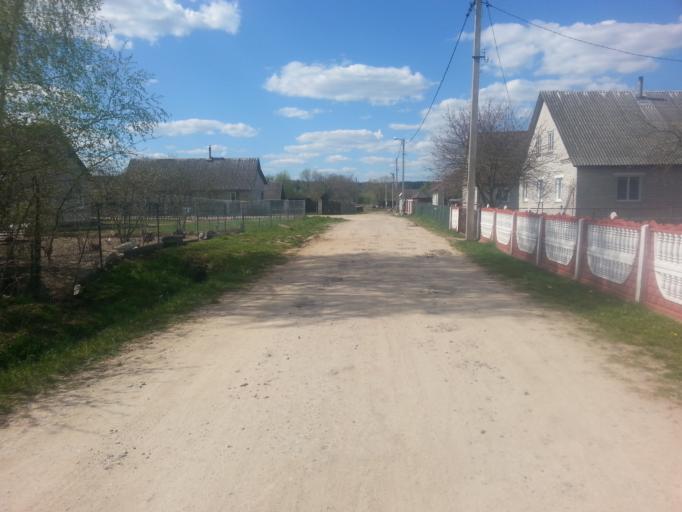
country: BY
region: Minsk
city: Narach
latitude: 54.9421
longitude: 26.6905
